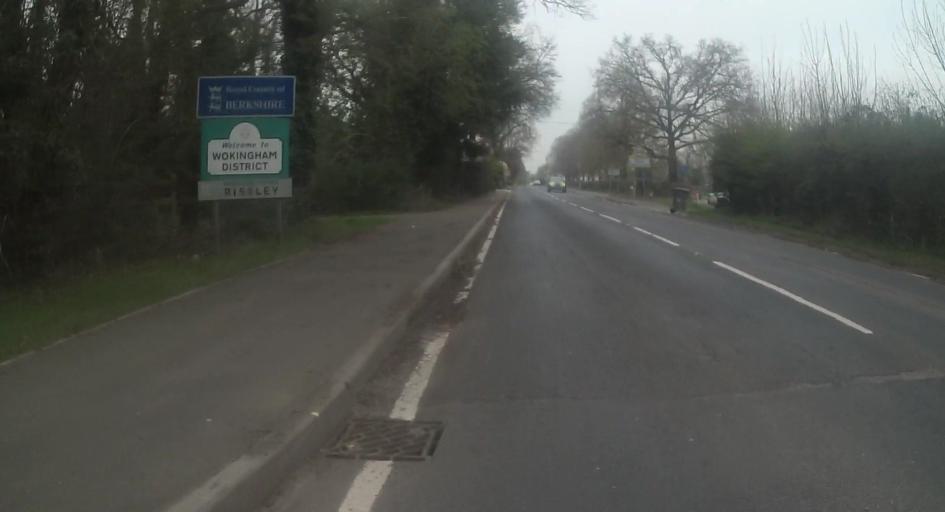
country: GB
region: England
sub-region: Wokingham
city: Swallowfield
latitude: 51.3610
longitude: -0.9630
